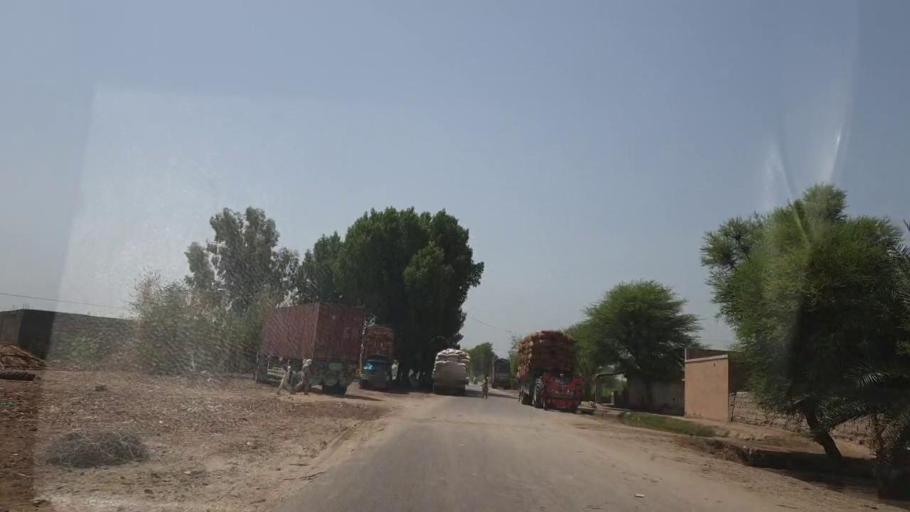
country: PK
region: Sindh
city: Ranipur
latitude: 27.2909
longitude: 68.6049
